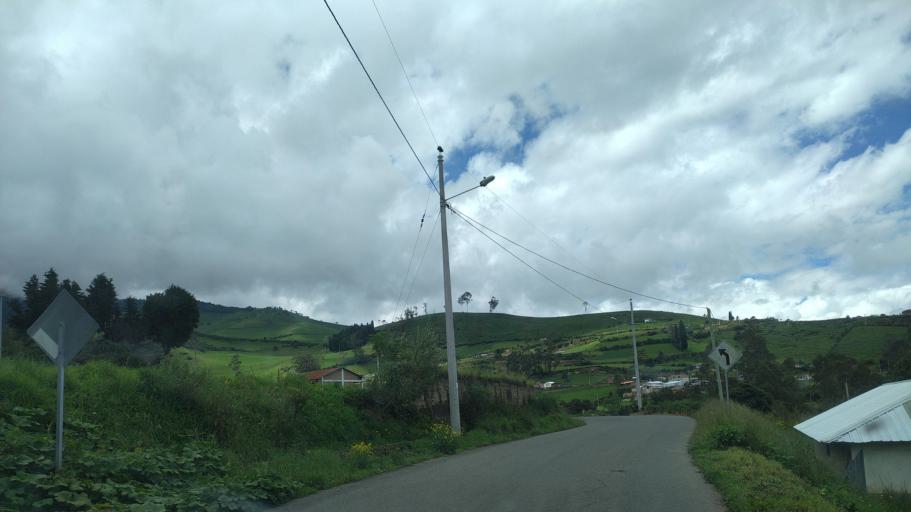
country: EC
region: Chimborazo
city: Riobamba
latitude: -1.6716
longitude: -78.5683
